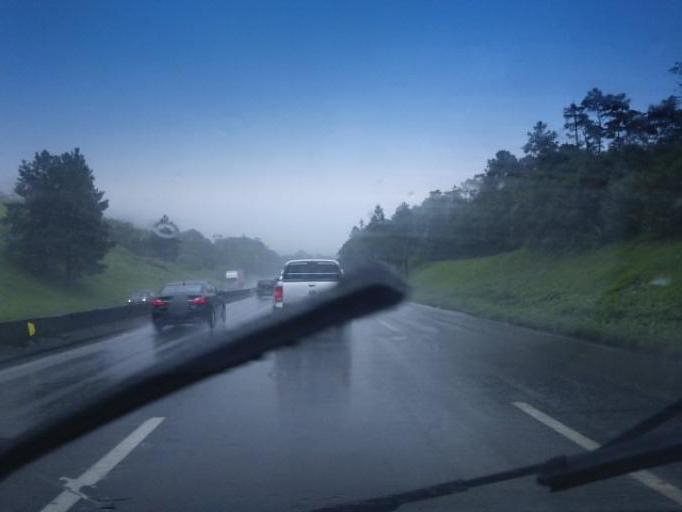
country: BR
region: Parana
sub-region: Guaratuba
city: Guaratuba
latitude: -25.8947
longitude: -48.9306
